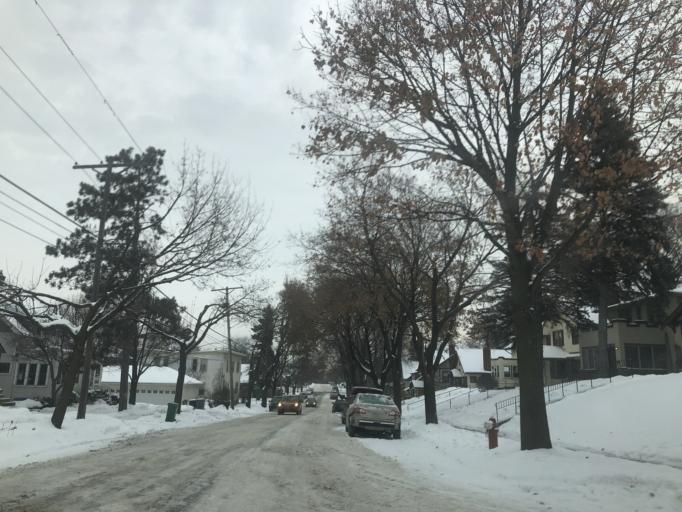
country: US
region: Minnesota
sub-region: Hennepin County
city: Richfield
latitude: 44.9160
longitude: -93.2806
